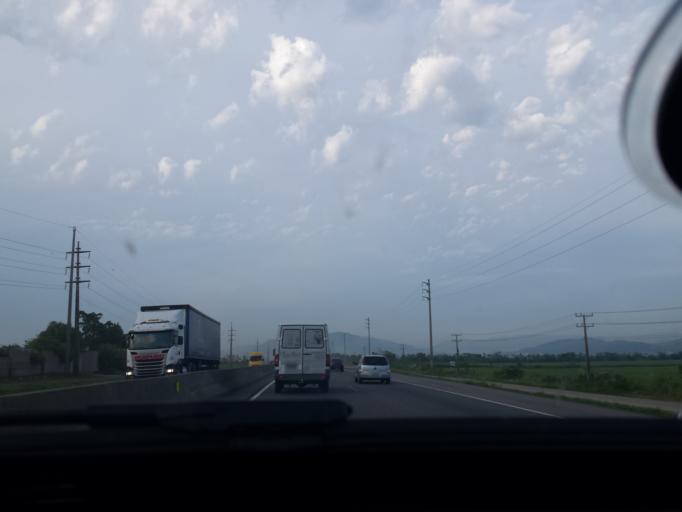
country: BR
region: Santa Catarina
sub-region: Tubarao
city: Tubarao
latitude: -28.4559
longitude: -48.9819
